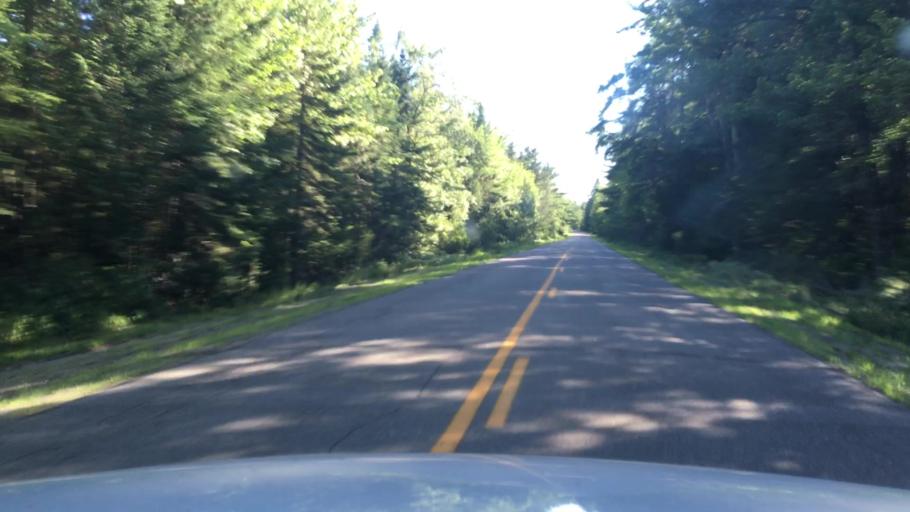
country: US
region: Maine
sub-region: Penobscot County
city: Enfield
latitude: 45.2054
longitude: -68.5945
